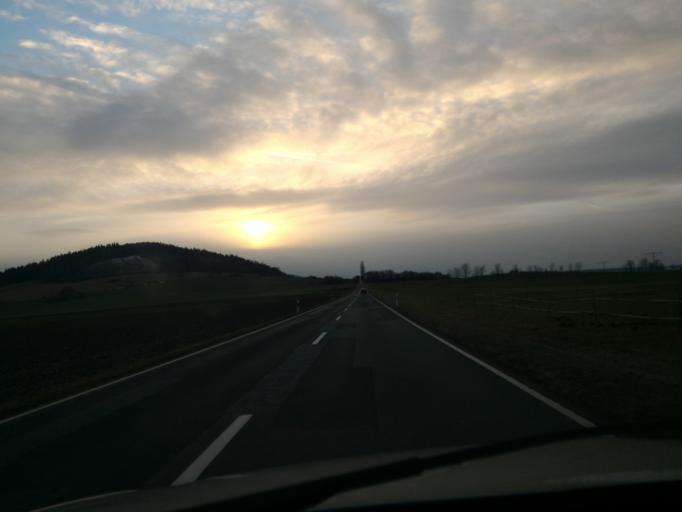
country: DE
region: Saxony
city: Bertsdorf-Hoernitz
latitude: 50.9015
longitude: 14.7209
